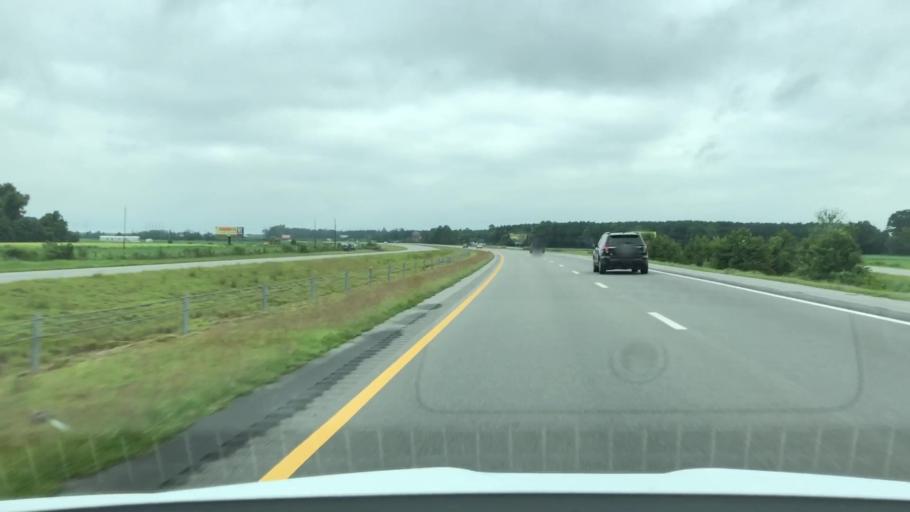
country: US
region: North Carolina
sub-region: Wayne County
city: Elroy
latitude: 35.3911
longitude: -77.8662
